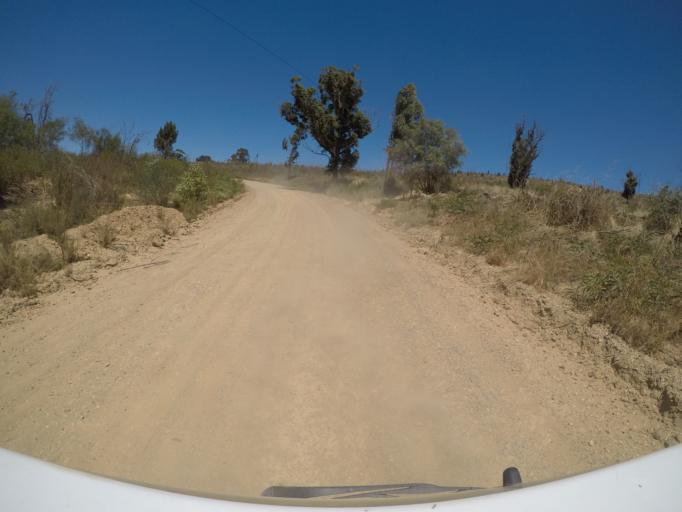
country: ZA
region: Western Cape
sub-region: Overberg District Municipality
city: Grabouw
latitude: -34.2183
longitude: 19.2040
